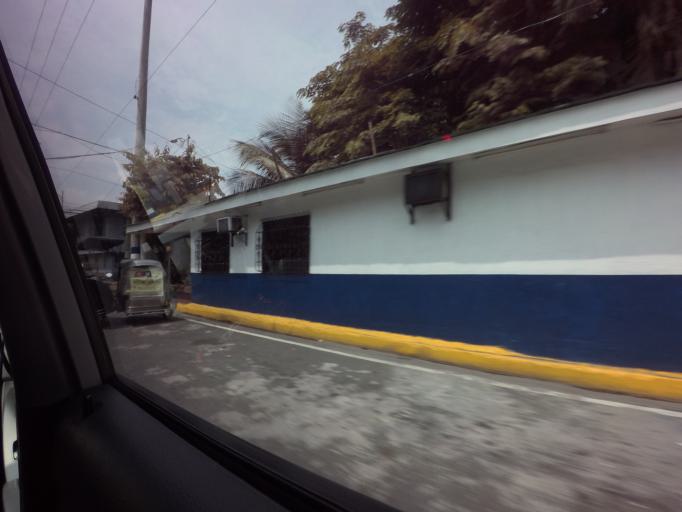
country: PH
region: Metro Manila
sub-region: City of Manila
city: Quiapo
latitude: 14.5744
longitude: 120.9935
